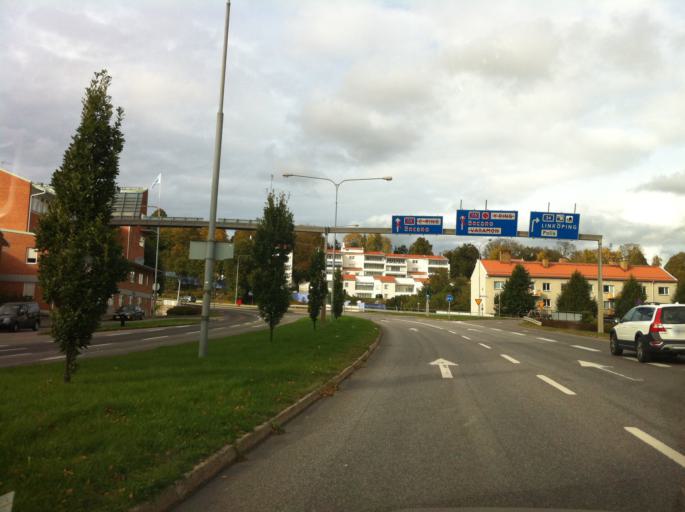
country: SE
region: OEstergoetland
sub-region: Motala Kommun
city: Motala
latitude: 58.5357
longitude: 15.0446
